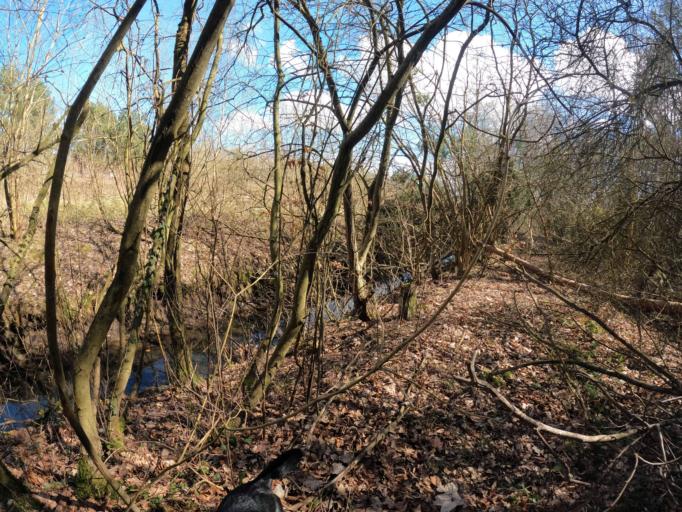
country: PL
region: West Pomeranian Voivodeship
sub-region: Powiat gryficki
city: Gryfice
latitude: 53.9242
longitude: 15.2310
